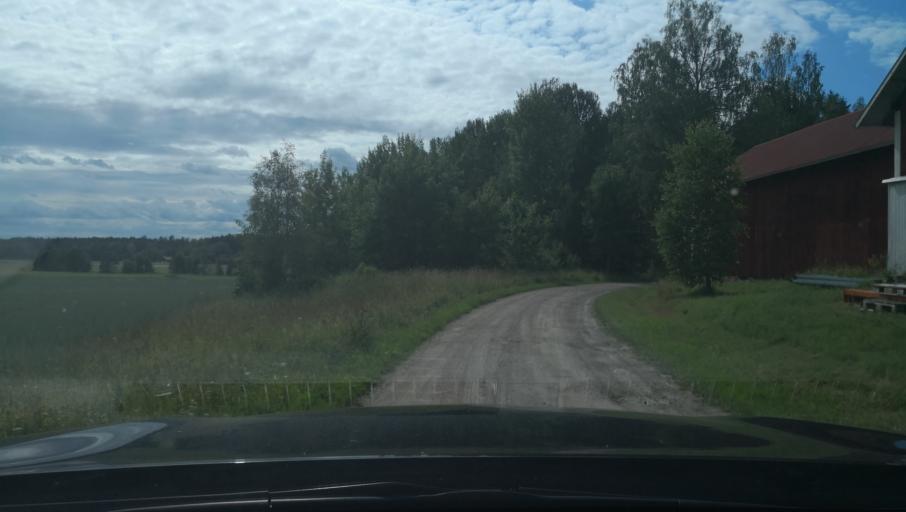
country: SE
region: Vaestmanland
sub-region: Kopings Kommun
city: Koping
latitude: 59.6401
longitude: 16.0674
